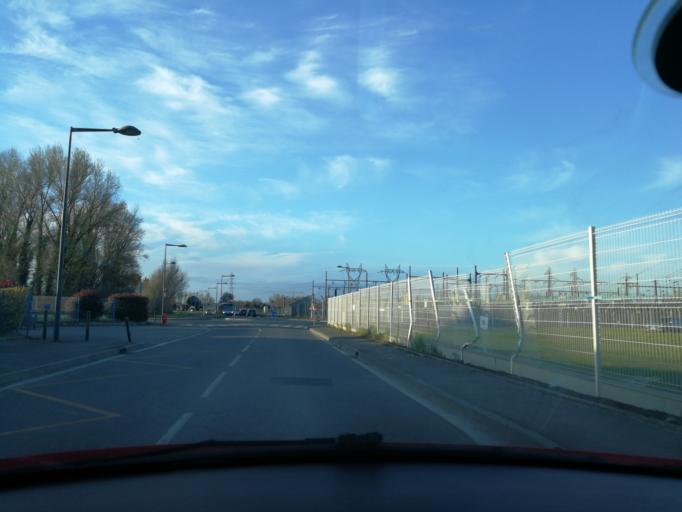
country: FR
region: Midi-Pyrenees
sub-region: Departement de la Haute-Garonne
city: Aucamville
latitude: 43.6562
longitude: 1.4115
